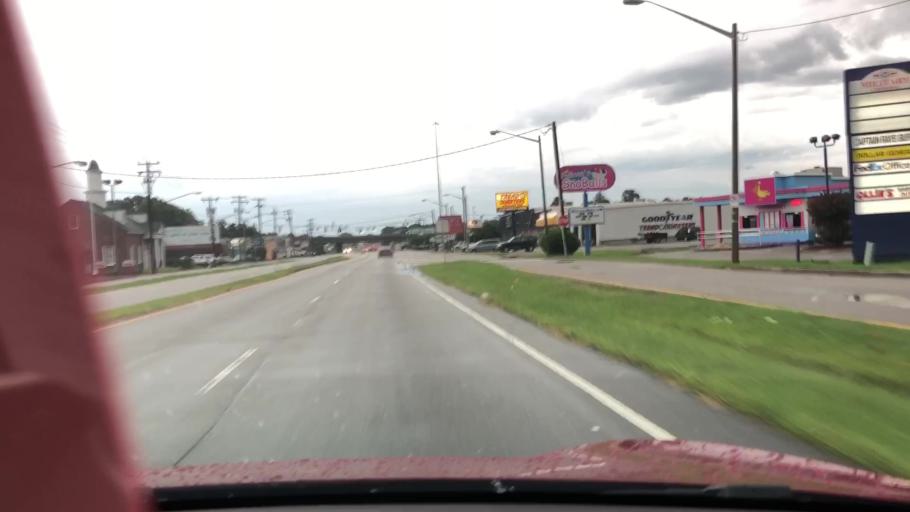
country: US
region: Virginia
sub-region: City of Chesapeake
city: Chesapeake
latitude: 36.8551
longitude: -76.2000
